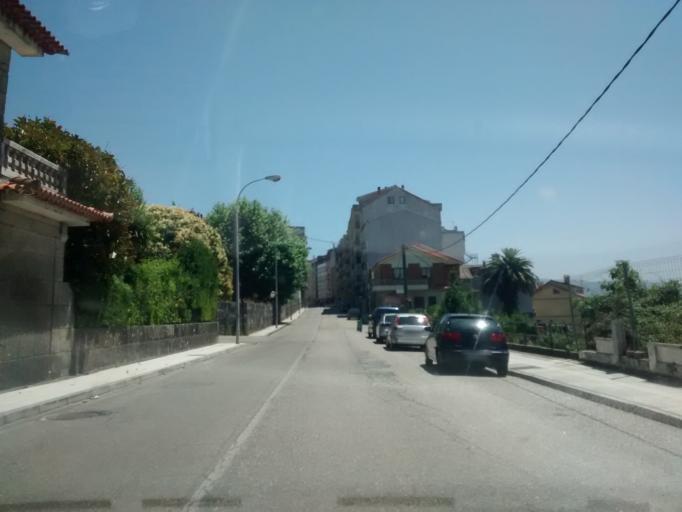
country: ES
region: Galicia
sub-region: Provincia de Pontevedra
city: Tui
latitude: 42.0507
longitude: -8.6492
